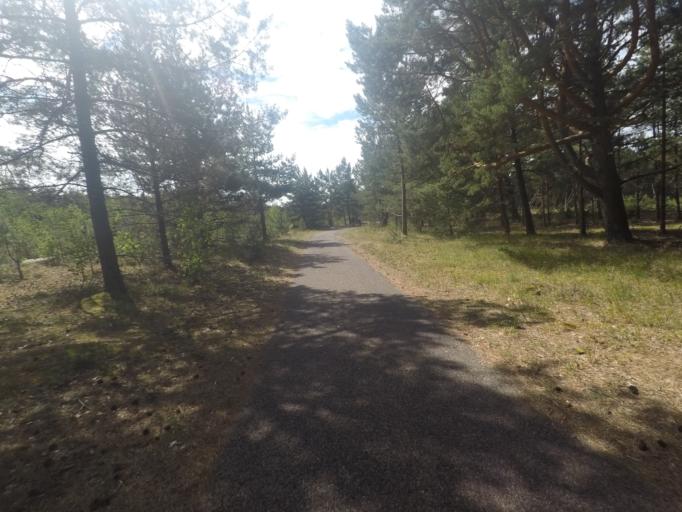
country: LT
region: Klaipedos apskritis
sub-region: Klaipeda
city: Klaipeda
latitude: 55.5708
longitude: 21.1133
